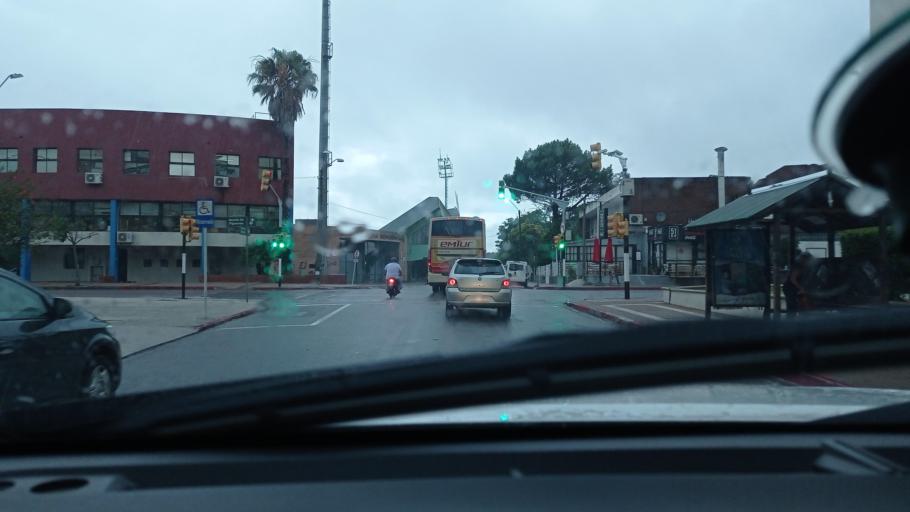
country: UY
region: Maldonado
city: Maldonado
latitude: -34.9149
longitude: -54.9568
